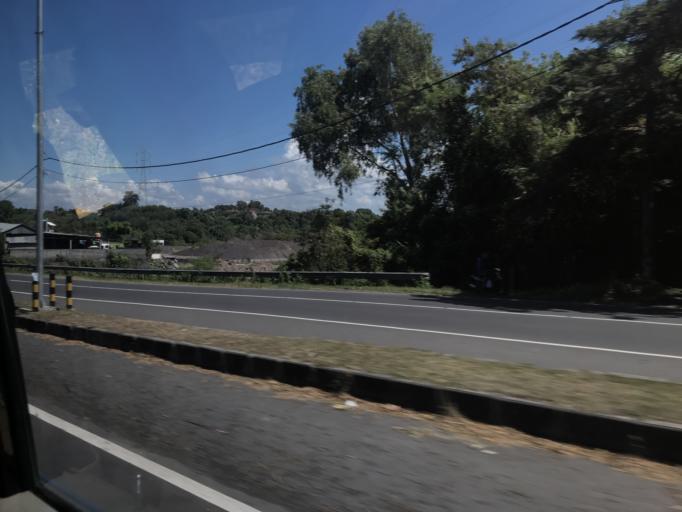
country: ID
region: Bali
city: Dawan
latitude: -8.5575
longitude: 115.4296
